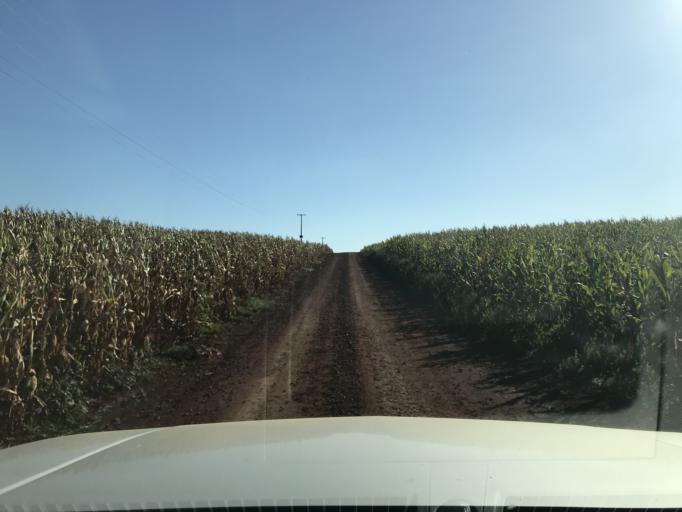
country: BR
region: Parana
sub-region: Palotina
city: Palotina
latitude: -24.2275
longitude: -53.8179
